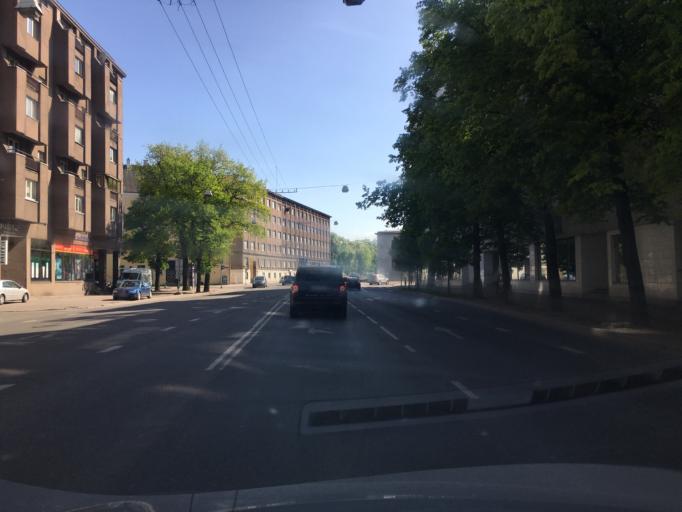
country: EE
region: Harju
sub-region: Tallinna linn
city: Tallinn
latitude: 59.4365
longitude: 24.7647
